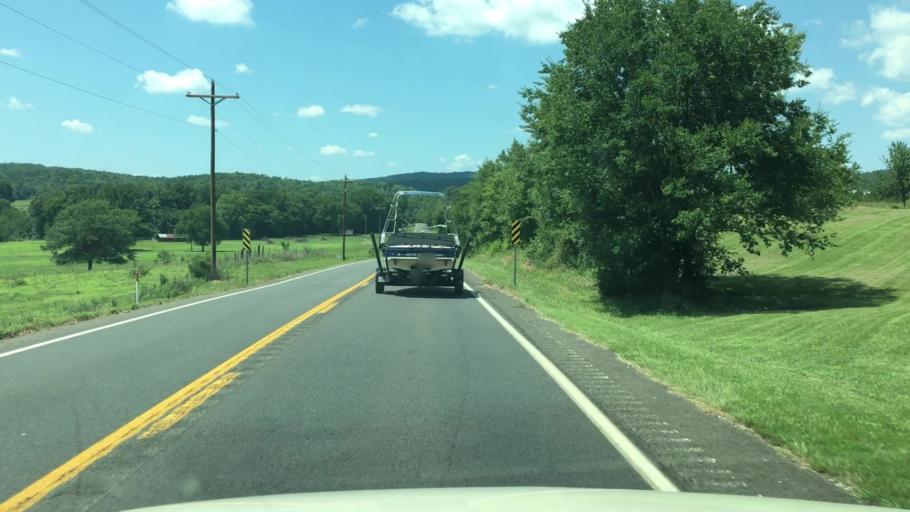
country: US
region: Arkansas
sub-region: Garland County
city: Lake Hamilton
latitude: 34.3323
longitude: -93.1762
